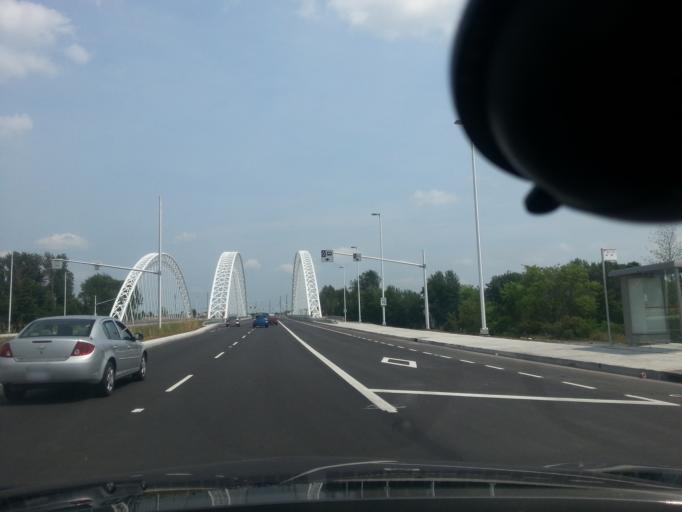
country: CA
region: Ontario
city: Bells Corners
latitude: 45.2704
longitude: -75.7050
